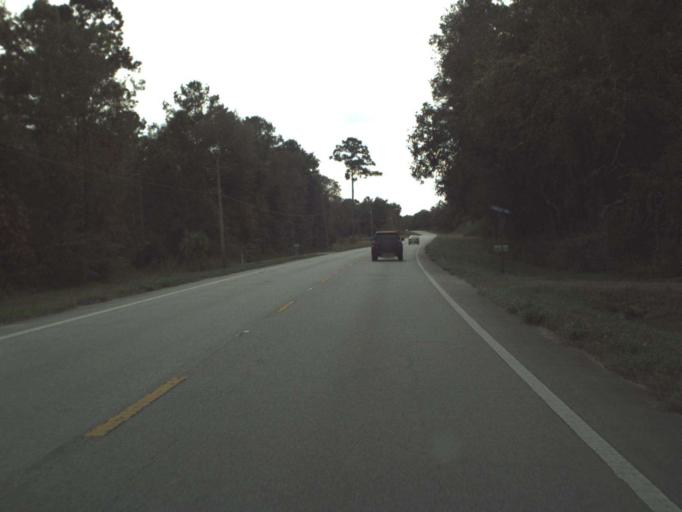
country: US
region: Florida
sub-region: Gadsden County
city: Quincy
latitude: 30.6423
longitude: -84.6001
